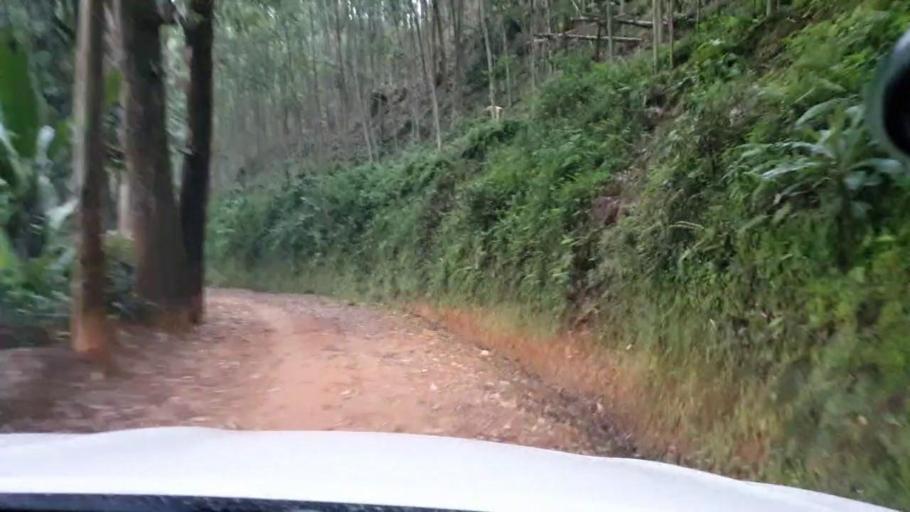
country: RW
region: Western Province
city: Cyangugu
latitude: -2.4102
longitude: 29.1942
